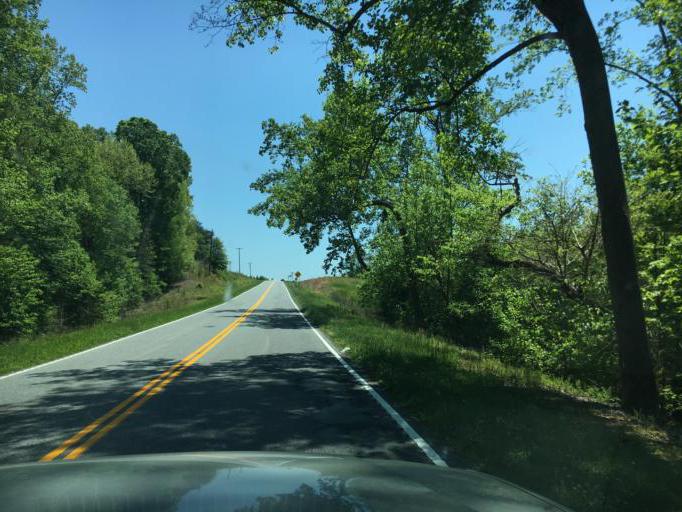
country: US
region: South Carolina
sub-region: Cherokee County
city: Blacksburg
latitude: 35.1539
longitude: -81.5748
